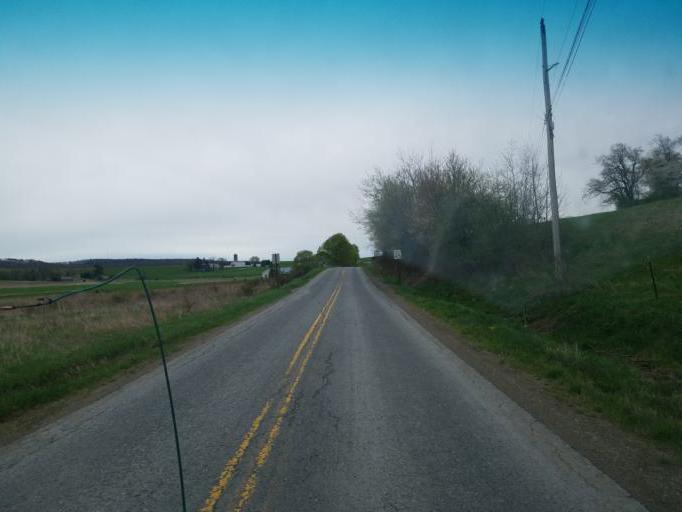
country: US
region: Pennsylvania
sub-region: Potter County
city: Galeton
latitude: 41.8920
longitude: -77.7449
